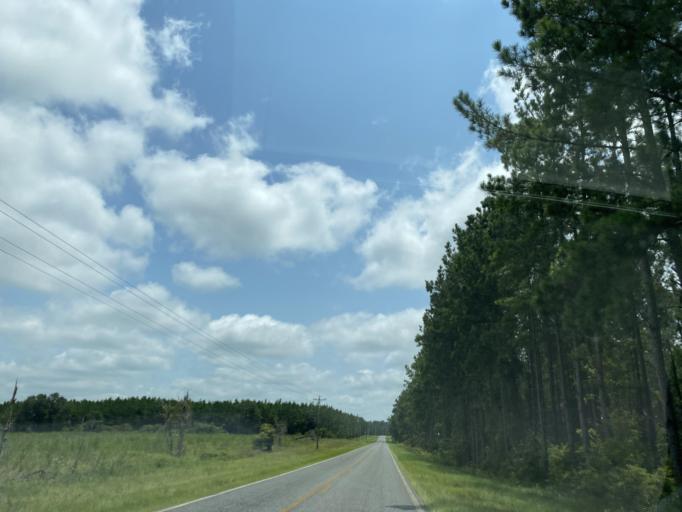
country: US
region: Georgia
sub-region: Wheeler County
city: Alamo
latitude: 32.1114
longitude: -82.7805
